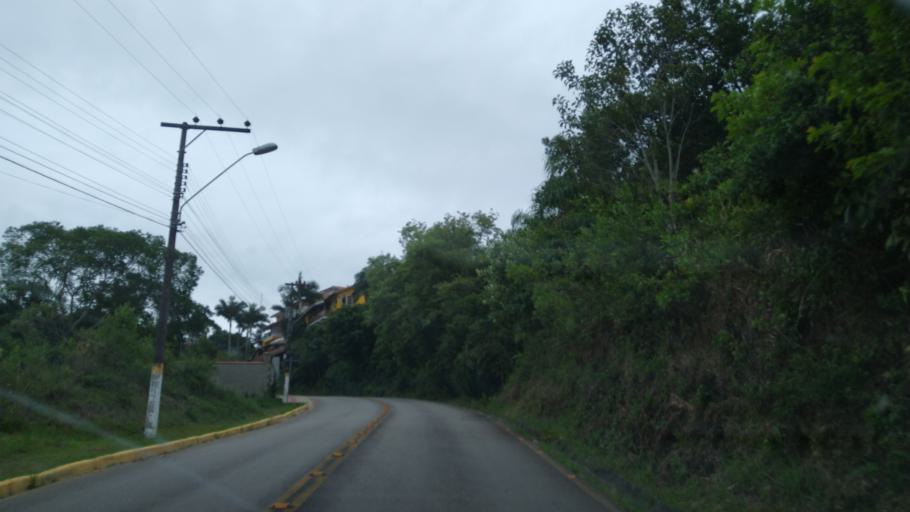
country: BR
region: Santa Catarina
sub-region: Itapema
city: Itapema
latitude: -27.0893
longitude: -48.6023
